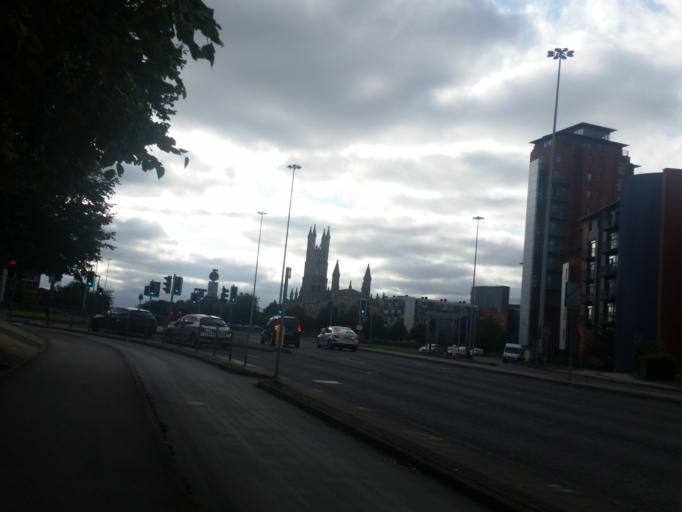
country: GB
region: England
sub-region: Manchester
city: Hulme
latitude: 53.4725
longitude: -2.2559
